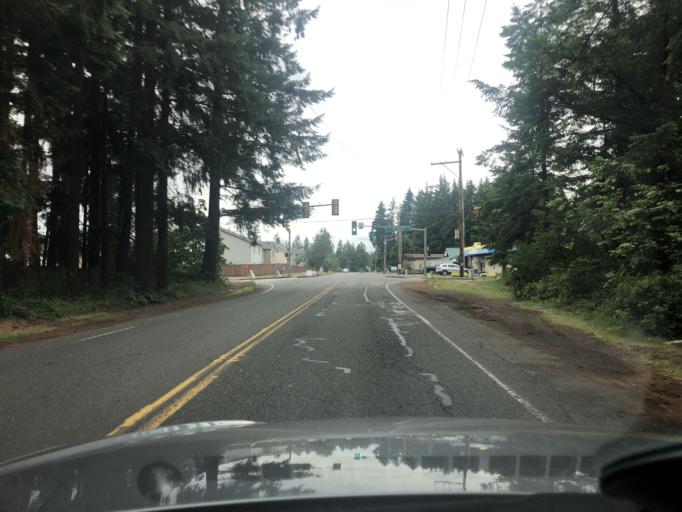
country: US
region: Washington
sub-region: King County
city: Lake Morton-Berrydale
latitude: 47.3400
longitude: -122.0539
